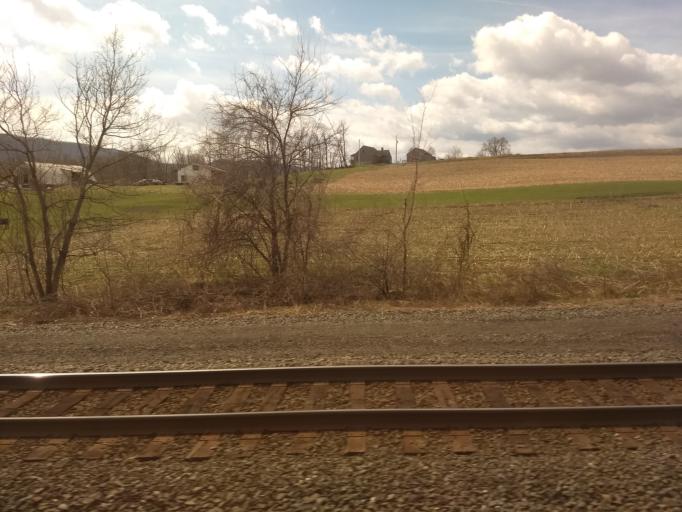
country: US
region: Pennsylvania
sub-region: Mifflin County
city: Belleville
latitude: 40.5123
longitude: -77.6886
